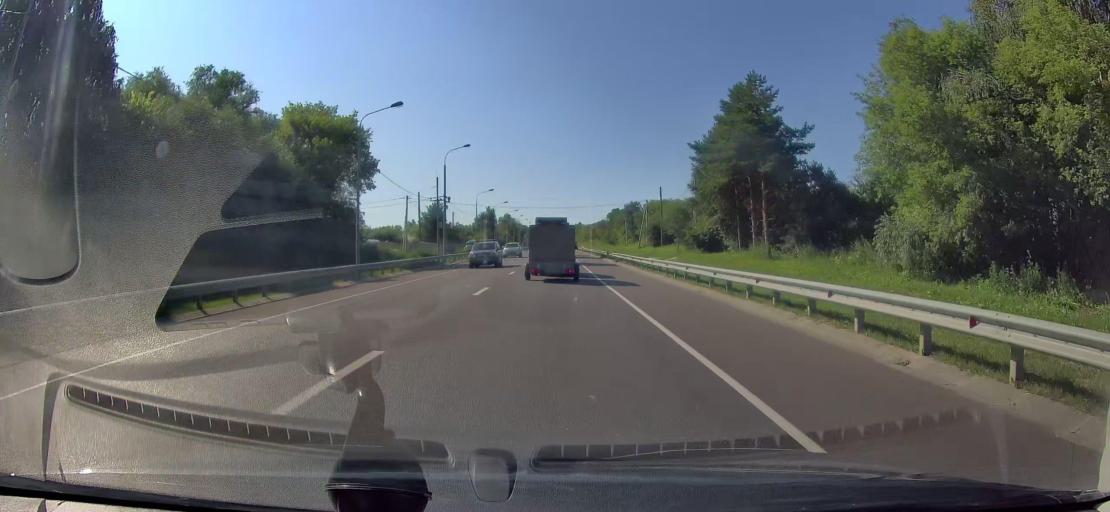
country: RU
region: Orjol
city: Kromy
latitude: 52.6207
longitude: 35.7593
